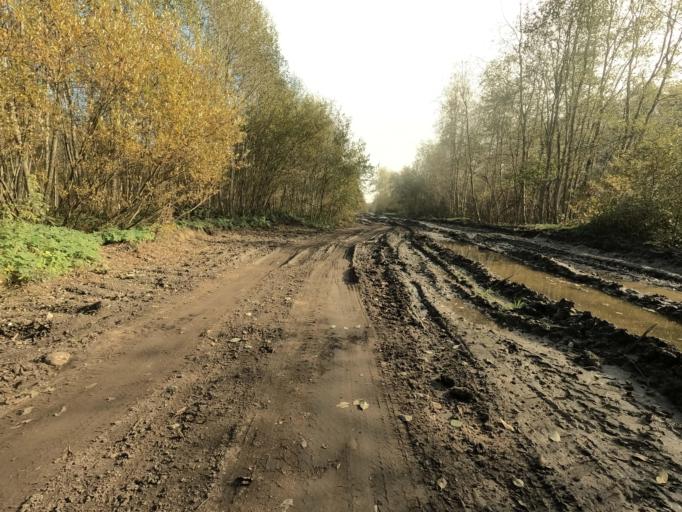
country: RU
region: Novgorod
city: Batetskiy
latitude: 58.8798
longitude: 30.7340
